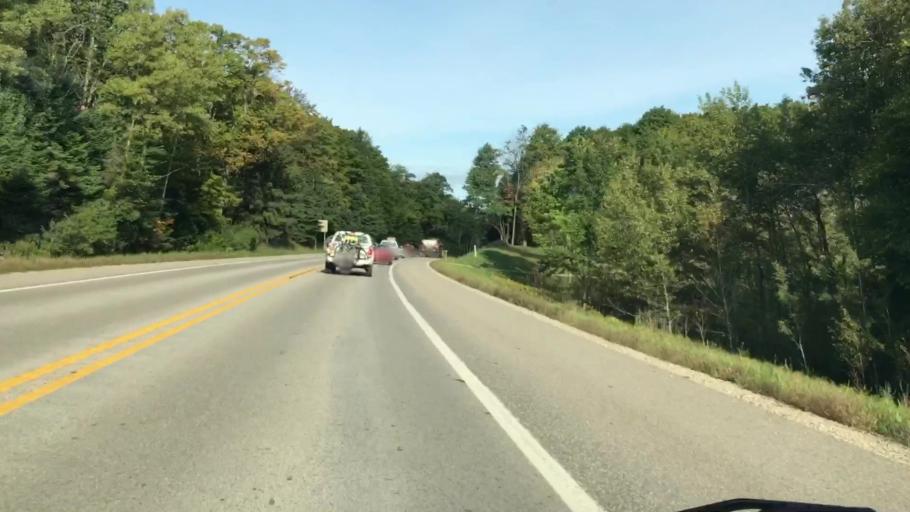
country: US
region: Michigan
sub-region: Luce County
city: Newberry
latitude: 46.3047
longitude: -85.5165
